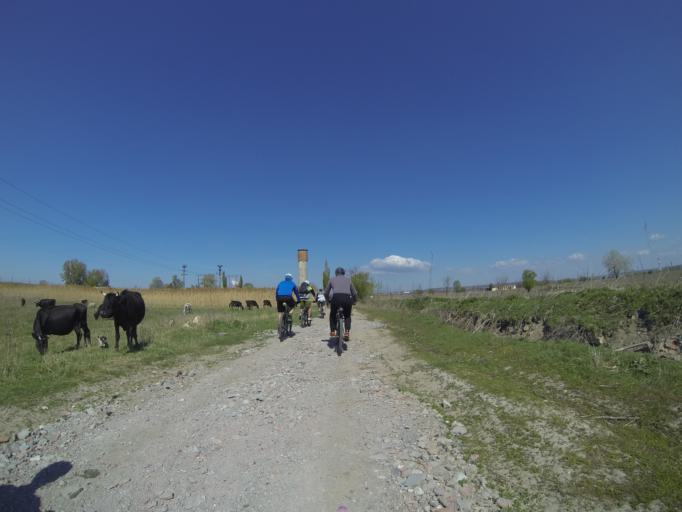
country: RO
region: Dolj
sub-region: Comuna Isalnita
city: Isalnita
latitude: 44.3681
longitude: 23.7457
